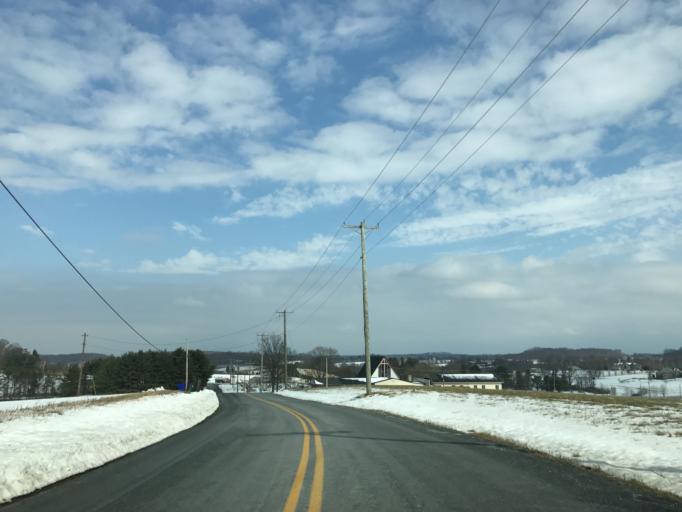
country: US
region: Maryland
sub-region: Harford County
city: Bel Air North
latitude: 39.6507
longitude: -76.3395
